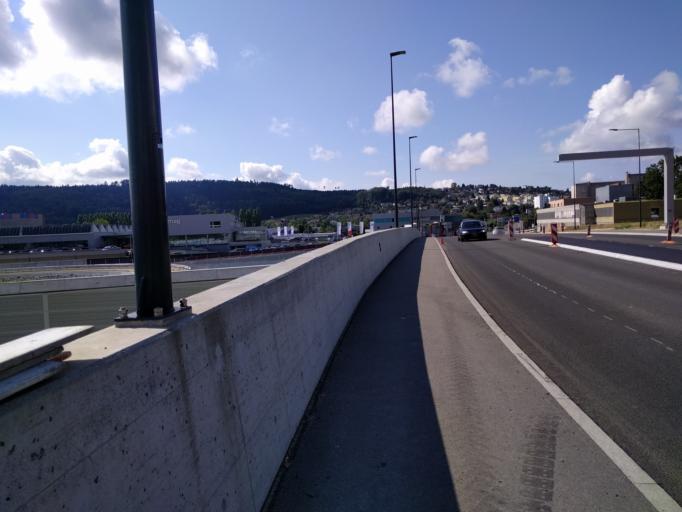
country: CH
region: Bern
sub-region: Biel/Bienne District
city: Brugg
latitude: 47.1235
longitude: 7.2605
